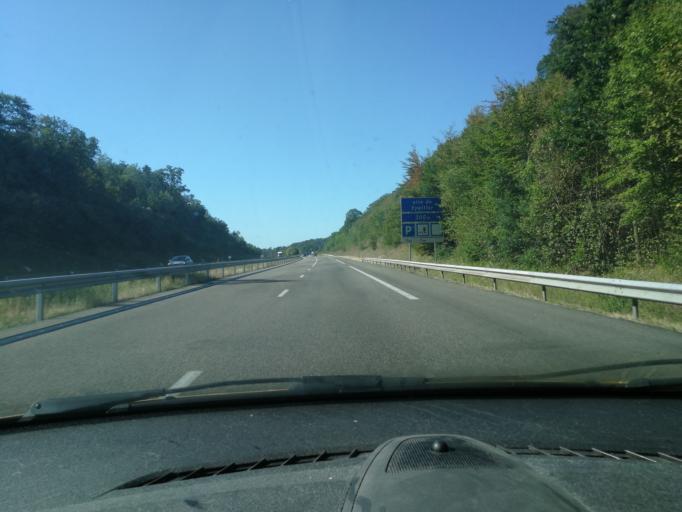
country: FR
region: Alsace
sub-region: Departement du Bas-Rhin
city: Sarrewerden
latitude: 48.8864
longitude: 7.1217
